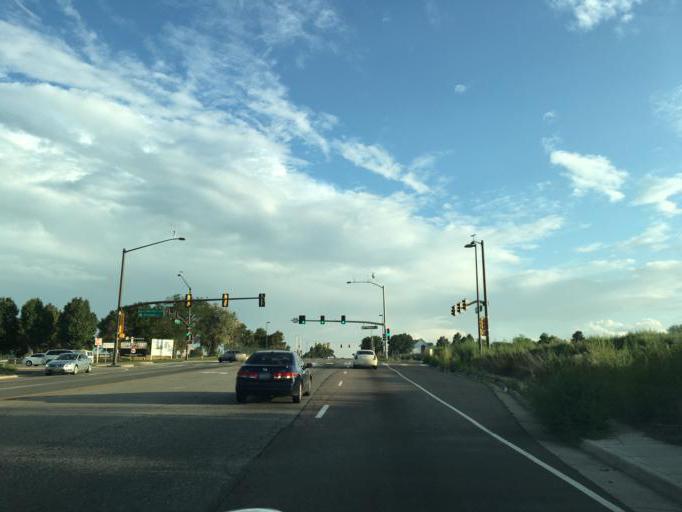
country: US
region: Colorado
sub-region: Adams County
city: Aurora
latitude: 39.7555
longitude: -104.8470
